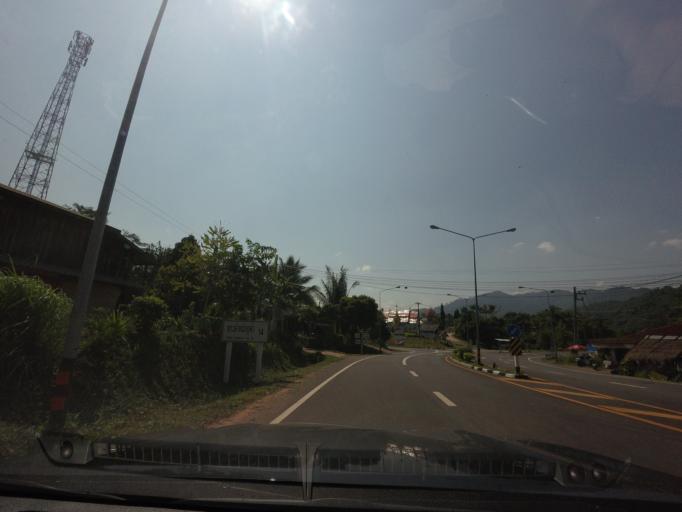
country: TH
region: Nan
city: Bo Kluea
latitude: 19.0823
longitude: 101.1535
